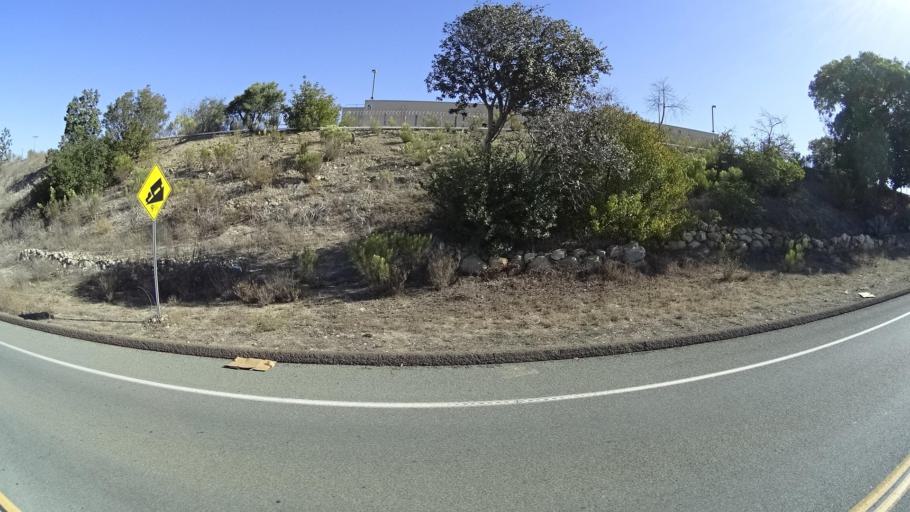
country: MX
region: Baja California
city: Tijuana
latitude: 32.5897
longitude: -116.9228
